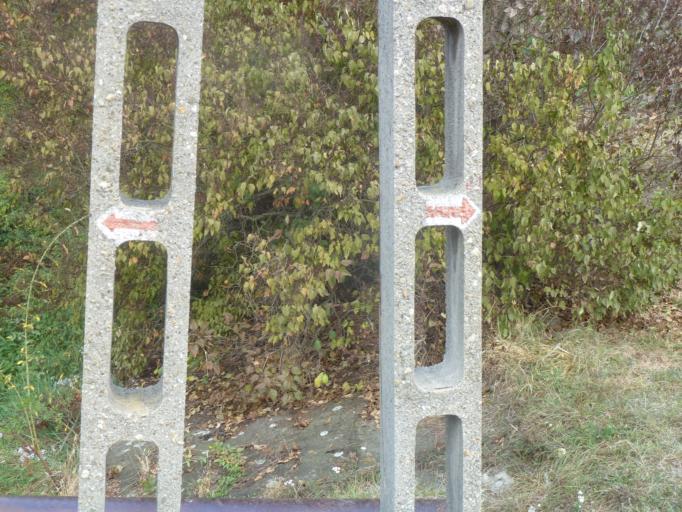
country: HU
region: Nograd
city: Kazar
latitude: 48.0495
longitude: 19.8605
